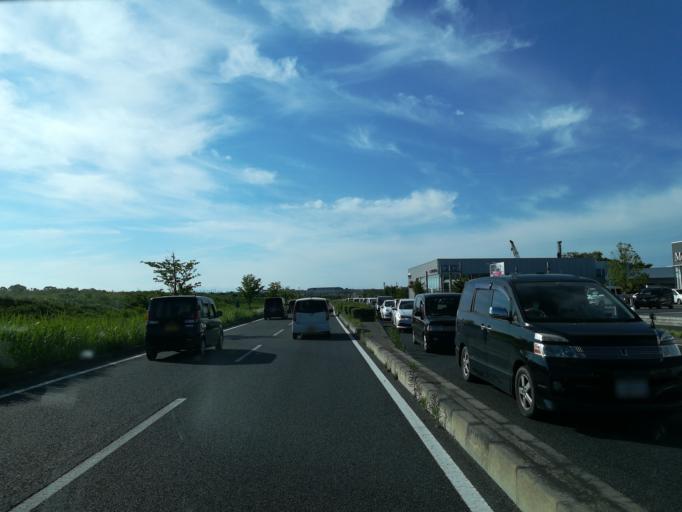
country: JP
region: Ibaraki
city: Naka
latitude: 36.0899
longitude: 140.0843
